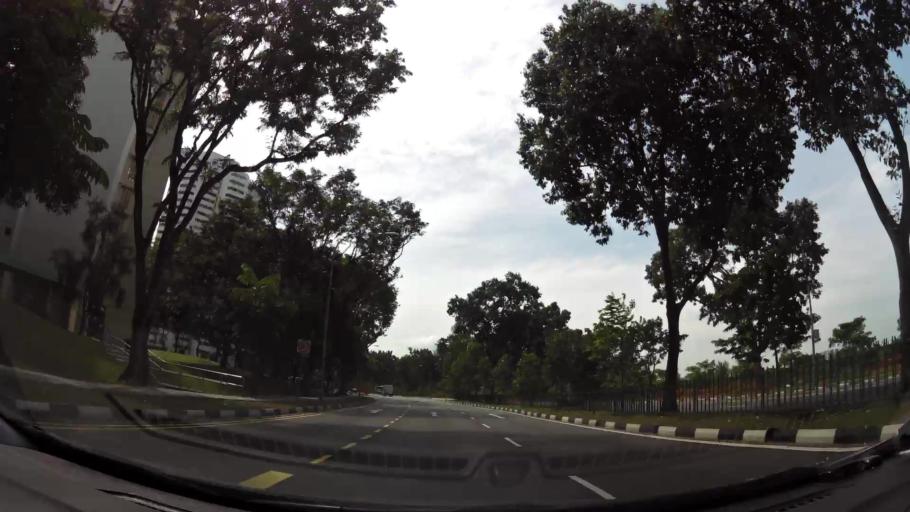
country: SG
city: Singapore
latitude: 1.3390
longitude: 103.7341
